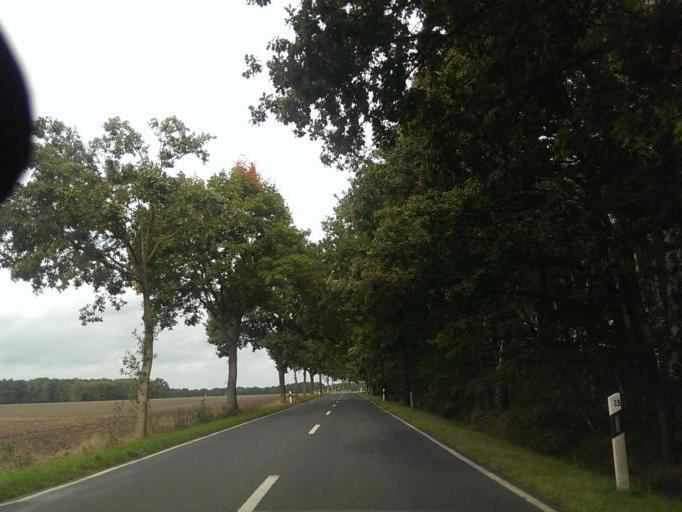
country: DE
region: Lower Saxony
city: Elze
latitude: 52.5321
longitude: 9.6882
